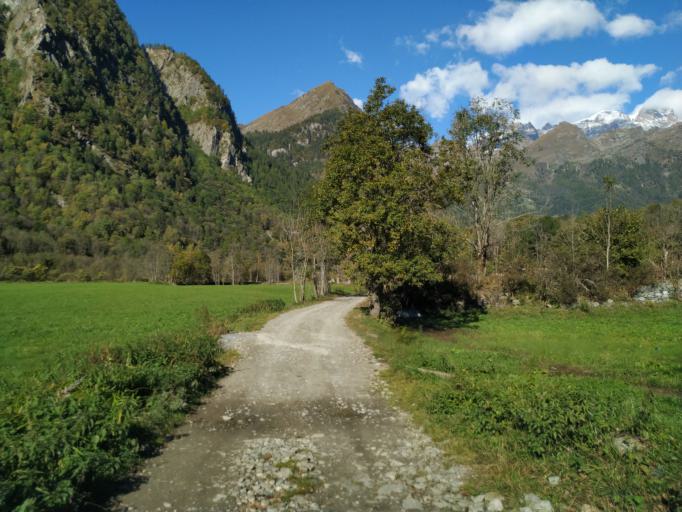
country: IT
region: Piedmont
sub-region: Provincia di Vercelli
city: Riva Valdobbia
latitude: 45.8401
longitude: 7.9495
